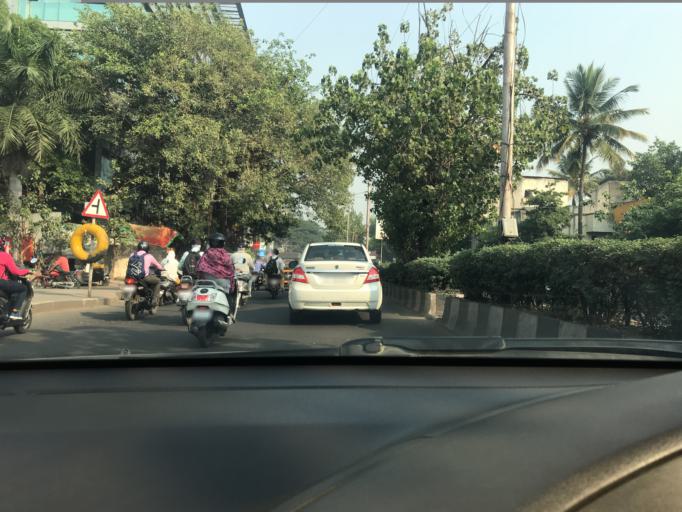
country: IN
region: Maharashtra
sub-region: Pune Division
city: Shivaji Nagar
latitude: 18.5302
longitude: 73.8300
